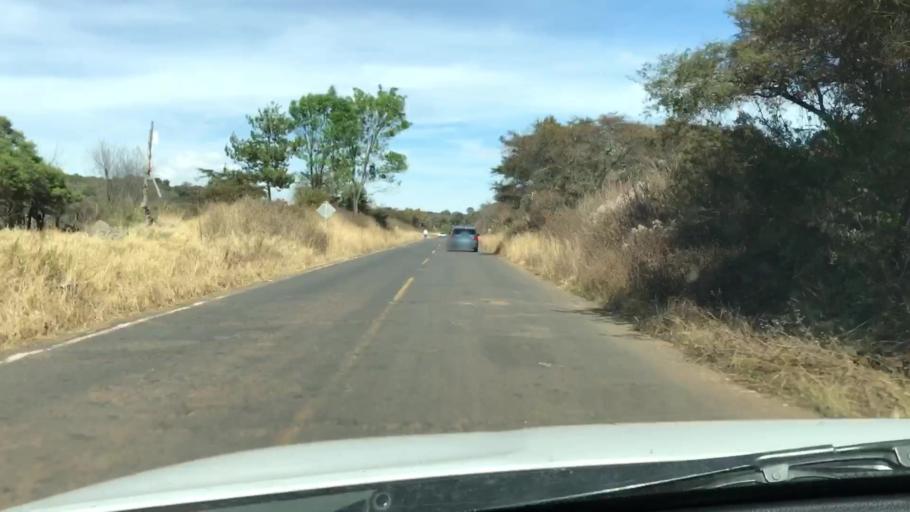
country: MX
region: Jalisco
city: Chiquilistlan
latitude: 20.1895
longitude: -103.7233
